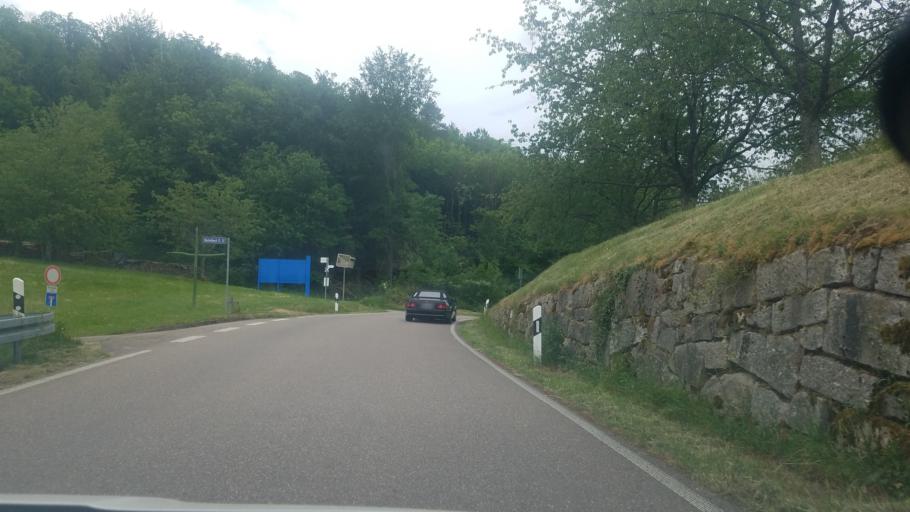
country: DE
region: Baden-Wuerttemberg
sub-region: Freiburg Region
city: Kappelrodeck
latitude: 48.6114
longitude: 8.1124
